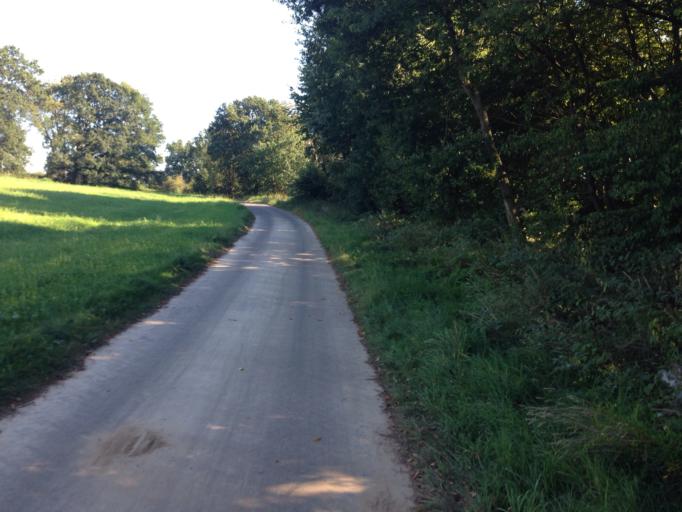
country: DE
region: Hesse
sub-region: Regierungsbezirk Giessen
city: Grunberg
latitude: 50.6183
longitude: 8.9478
